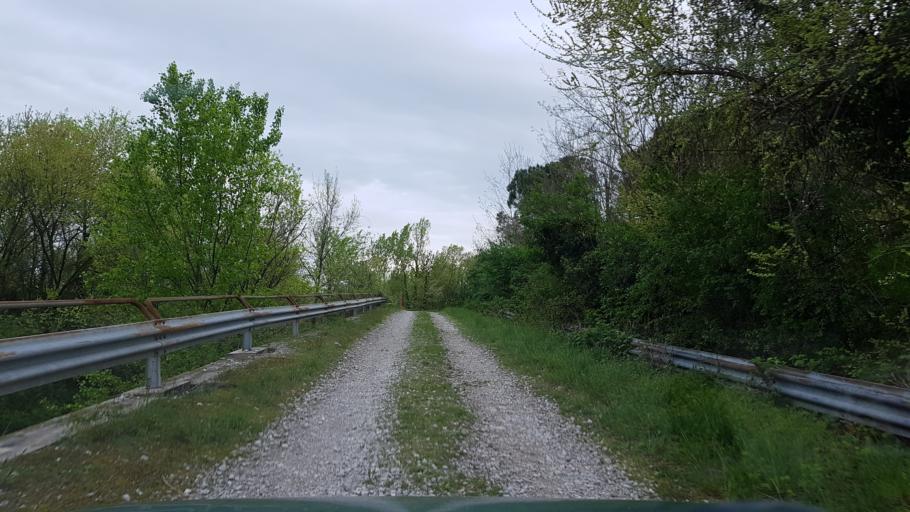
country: IT
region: Friuli Venezia Giulia
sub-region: Provincia di Gorizia
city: Mariano del Friuli
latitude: 45.9309
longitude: 13.4701
